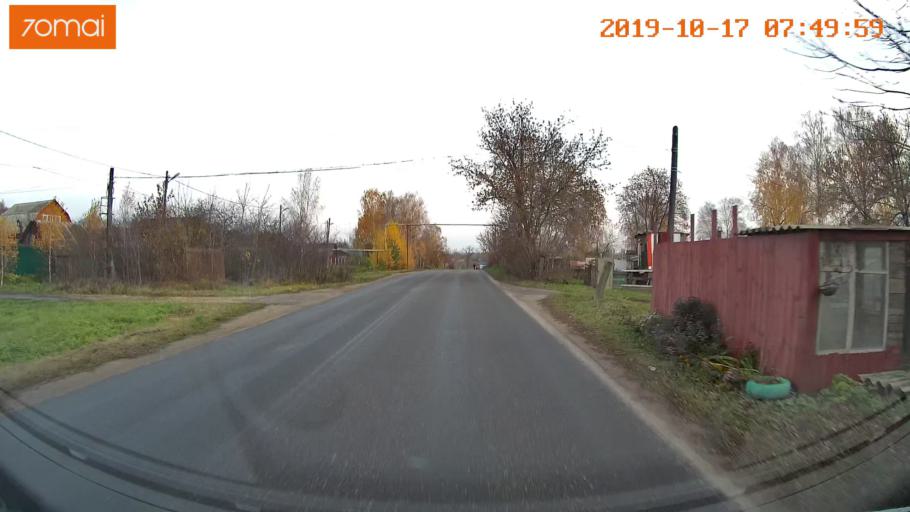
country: RU
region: Vladimir
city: Yur'yev-Pol'skiy
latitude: 56.4817
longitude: 39.6659
